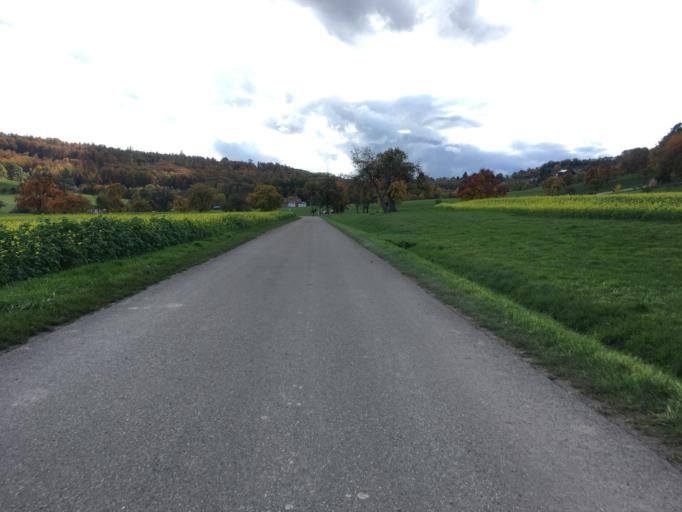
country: DE
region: Baden-Wuerttemberg
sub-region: Regierungsbezirk Stuttgart
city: Waldenburg
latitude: 49.1916
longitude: 9.6527
